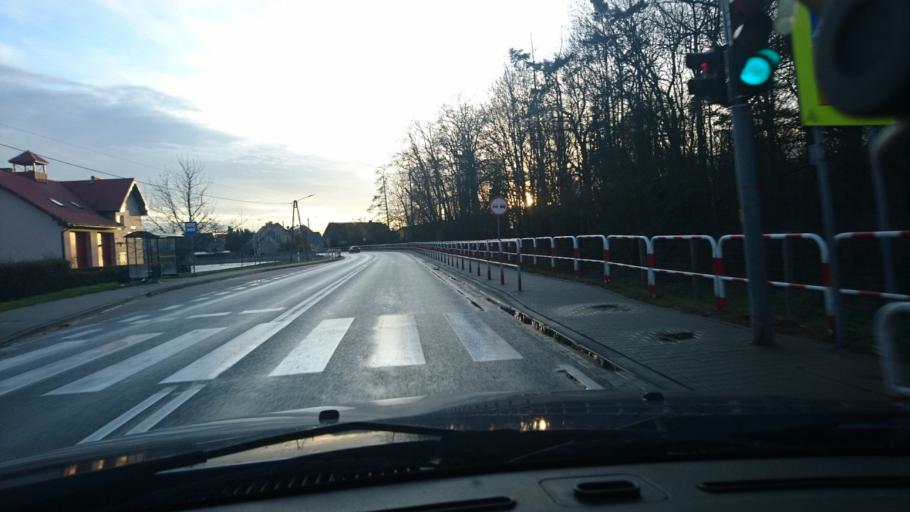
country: PL
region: Greater Poland Voivodeship
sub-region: Powiat kepinski
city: Opatow
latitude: 51.1811
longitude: 18.1443
